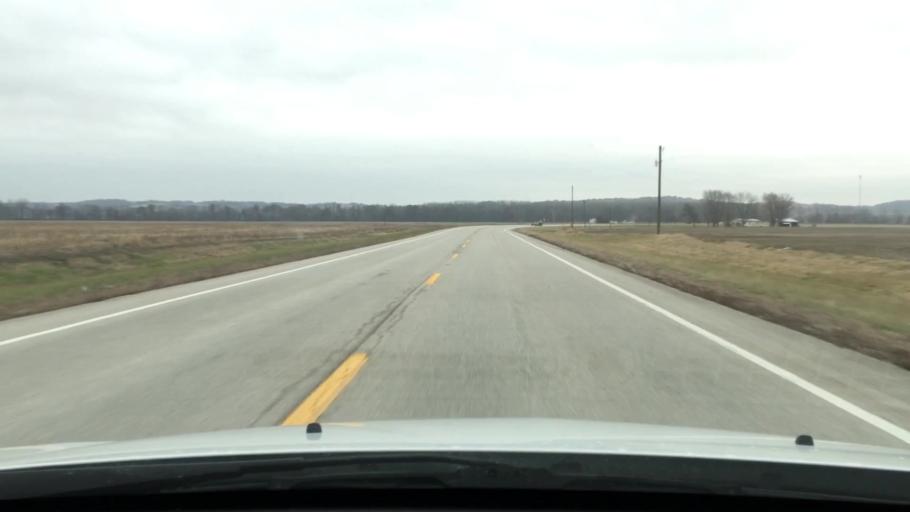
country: US
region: Missouri
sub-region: Pike County
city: Louisiana
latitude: 39.4967
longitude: -91.0023
